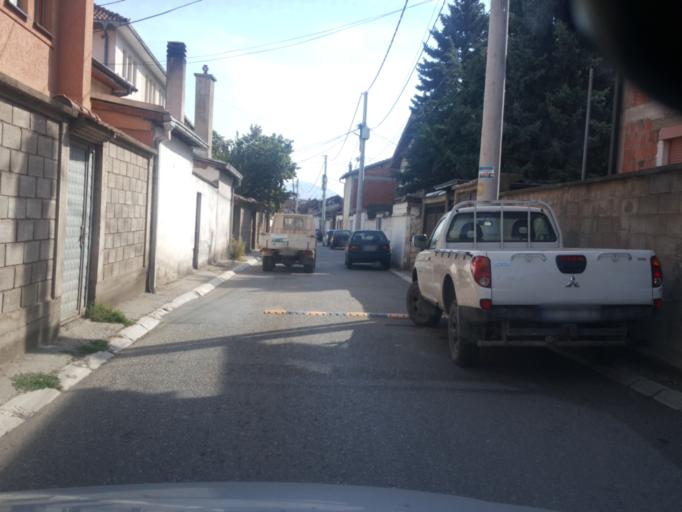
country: XK
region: Gjakova
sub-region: Komuna e Gjakoves
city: Gjakove
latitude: 42.3775
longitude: 20.4252
